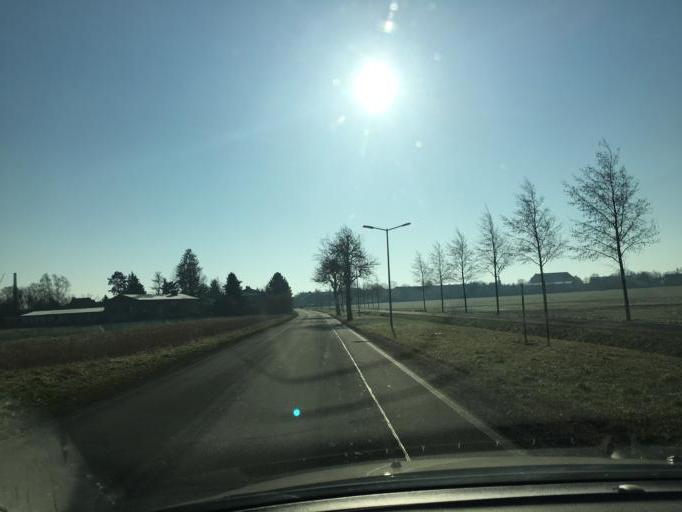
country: DE
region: Saxony
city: Grossposna
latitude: 51.2905
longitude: 12.4576
